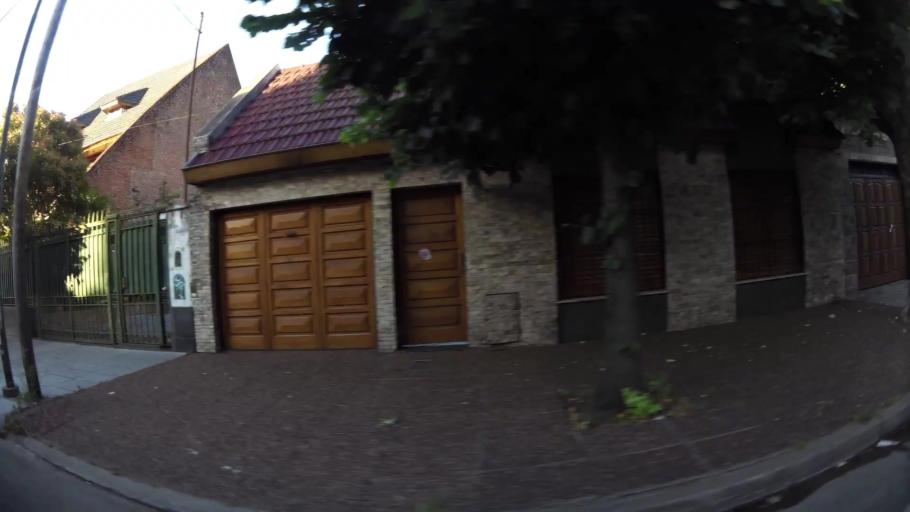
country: AR
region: Buenos Aires
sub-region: Partido de General San Martin
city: General San Martin
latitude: -34.5699
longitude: -58.5347
